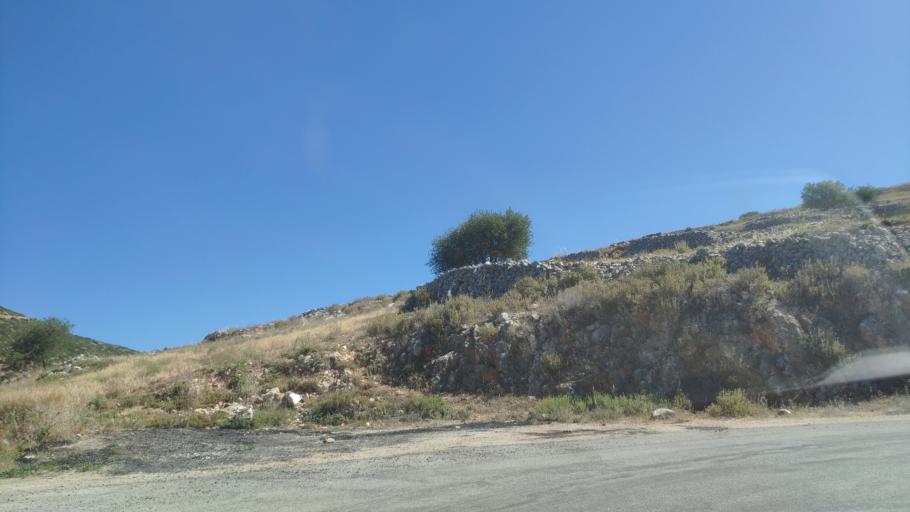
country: GR
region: Peloponnese
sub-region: Nomos Korinthias
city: Khiliomodhi
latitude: 37.7546
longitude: 22.8765
